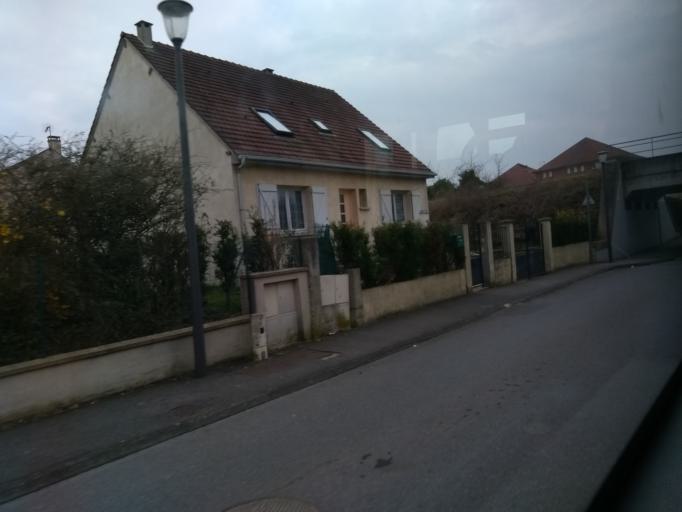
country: FR
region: Picardie
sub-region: Departement de l'Oise
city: Margny-les-Compiegne
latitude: 49.4220
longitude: 2.8109
